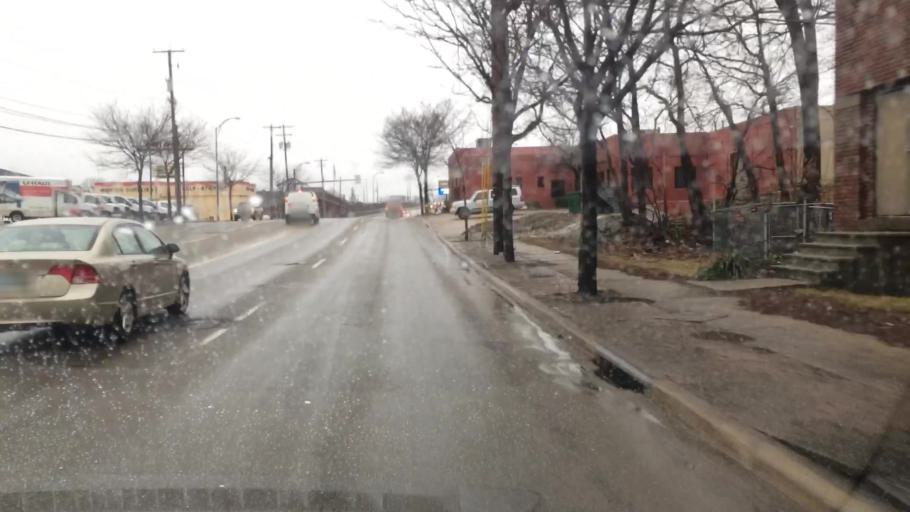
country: US
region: Ohio
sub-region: Summit County
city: Cuyahoga Falls
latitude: 41.1023
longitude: -81.4846
